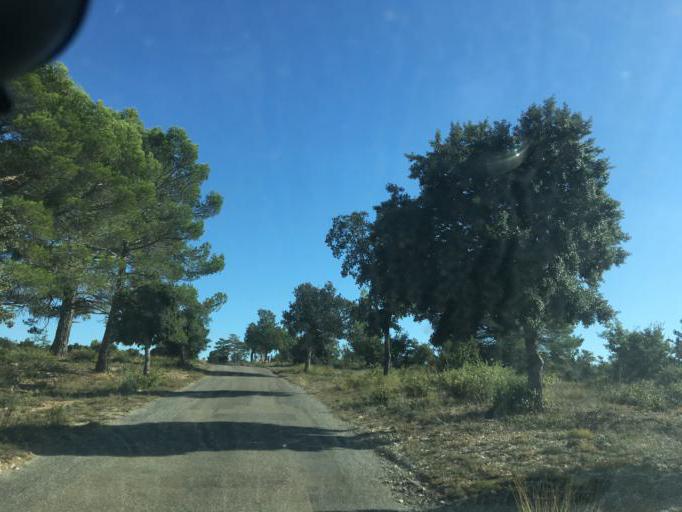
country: FR
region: Provence-Alpes-Cote d'Azur
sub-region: Departement des Alpes-de-Haute-Provence
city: Riez
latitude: 43.7375
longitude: 6.0991
